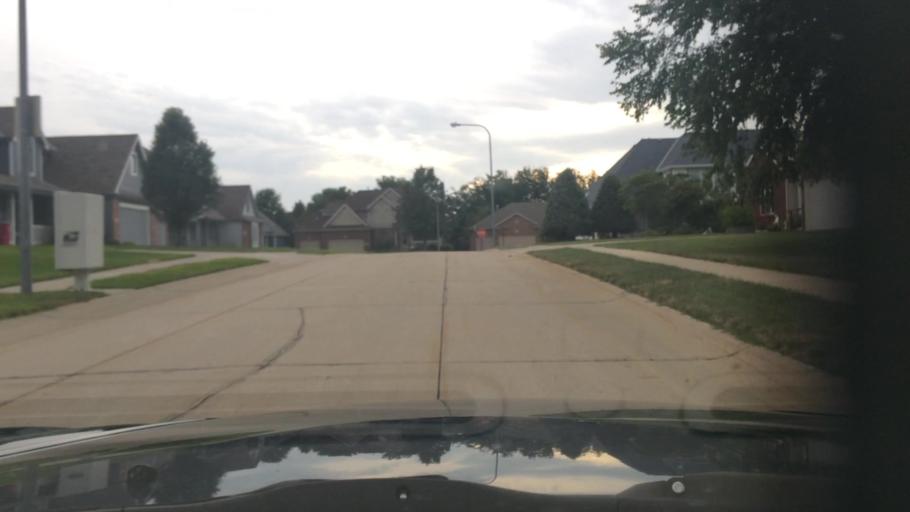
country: US
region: Nebraska
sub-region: Sarpy County
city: La Vista
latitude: 41.1813
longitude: -96.0534
